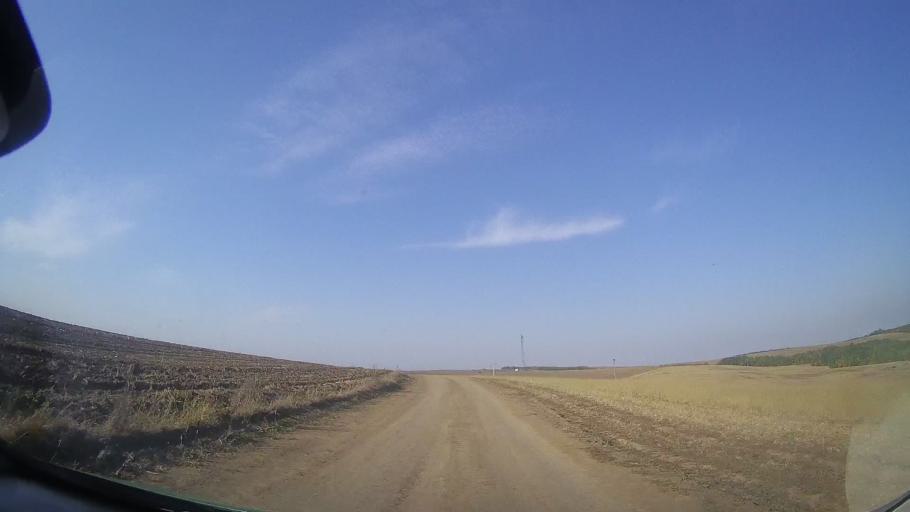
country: RO
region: Timis
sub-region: Oras Recas
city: Recas
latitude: 45.8816
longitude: 21.5501
